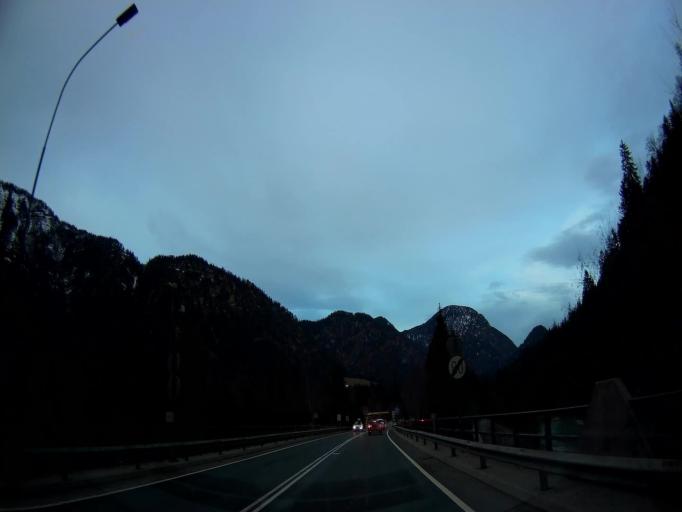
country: AT
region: Salzburg
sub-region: Politischer Bezirk Zell am See
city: Unken
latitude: 47.6519
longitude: 12.7388
